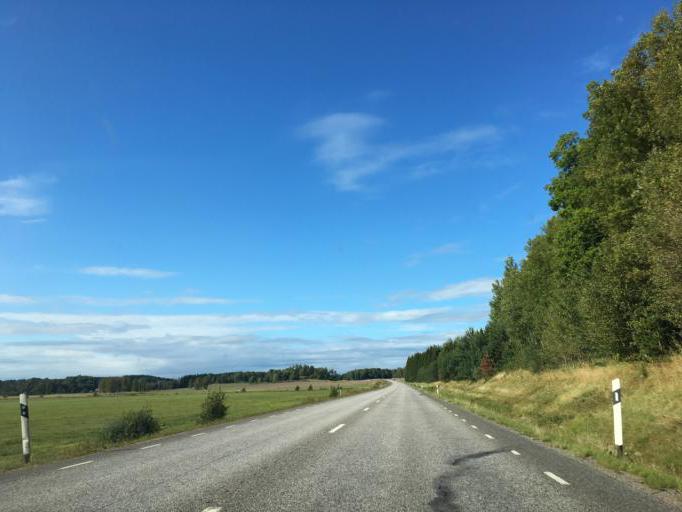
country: SE
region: Soedermanland
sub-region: Nykopings Kommun
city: Nykoping
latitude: 58.7932
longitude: 16.9550
